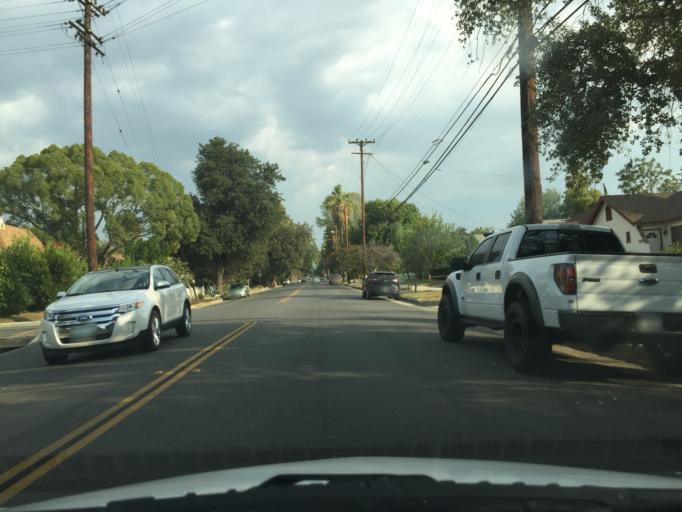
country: US
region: California
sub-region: San Bernardino County
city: Redlands
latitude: 34.0481
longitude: -117.1876
